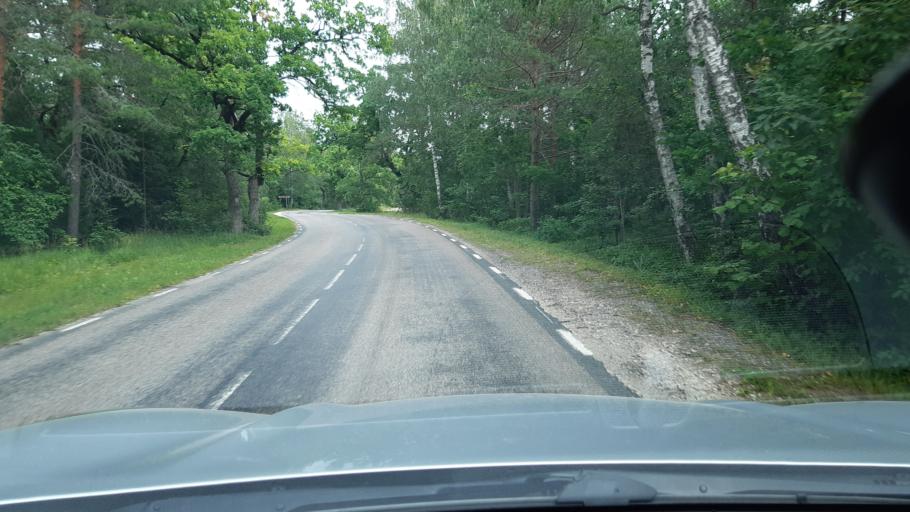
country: EE
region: Raplamaa
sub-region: Maerjamaa vald
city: Marjamaa
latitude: 59.0405
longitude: 24.5074
